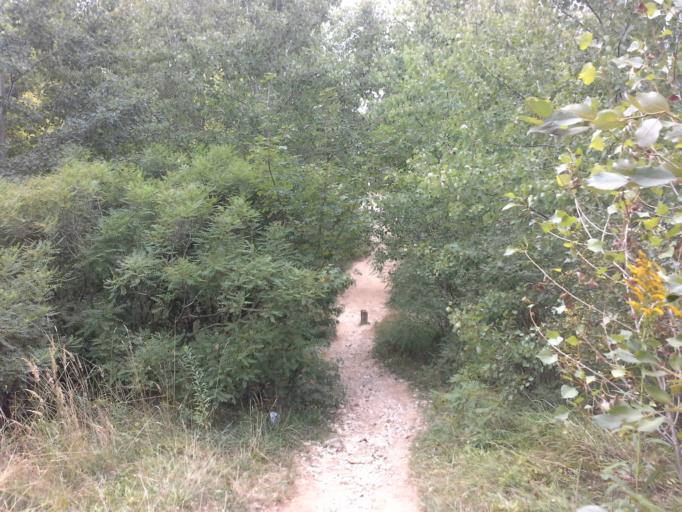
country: PL
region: Lesser Poland Voivodeship
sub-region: Powiat chrzanowski
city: Trzebinia
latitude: 50.1632
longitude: 19.4650
